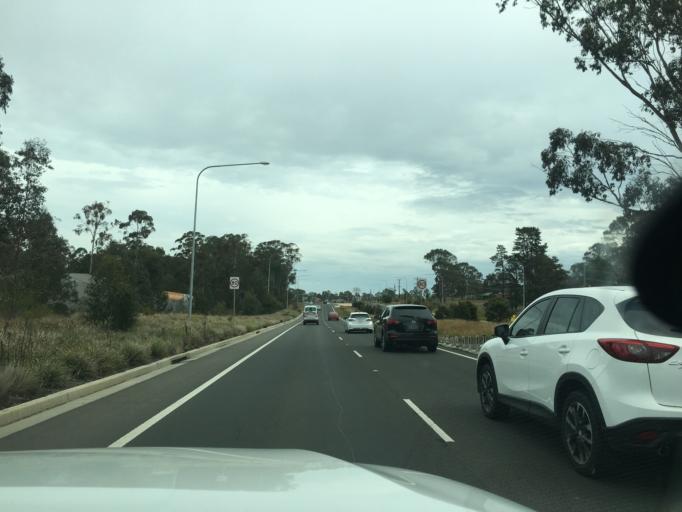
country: AU
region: New South Wales
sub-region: Campbelltown Municipality
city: Denham Court
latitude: -33.9802
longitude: 150.8030
